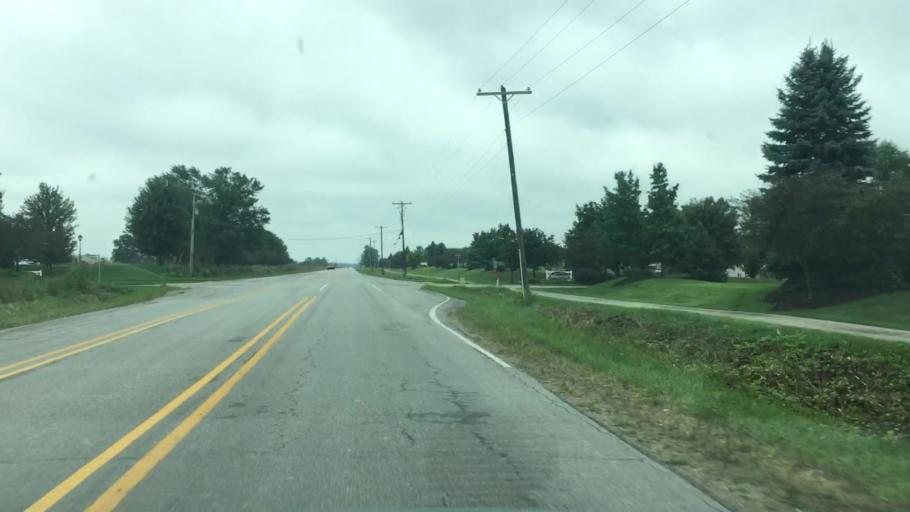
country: US
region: Michigan
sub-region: Ottawa County
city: Hudsonville
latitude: 42.8508
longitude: -85.8365
